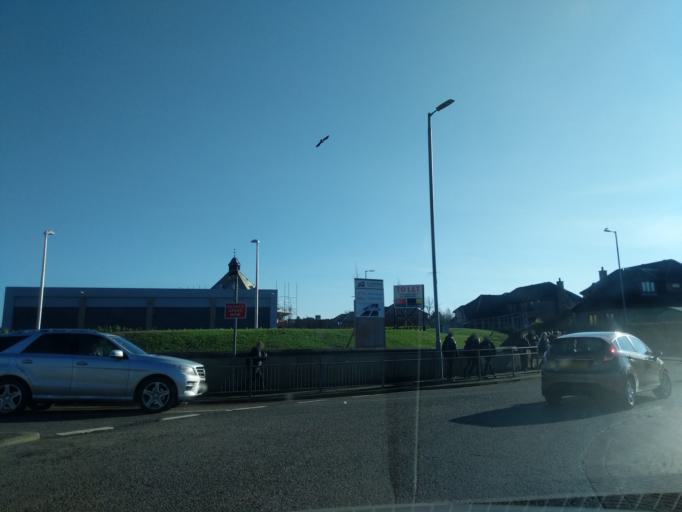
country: GB
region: Scotland
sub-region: South Lanarkshire
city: Lanark
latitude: 55.6712
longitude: -3.7709
